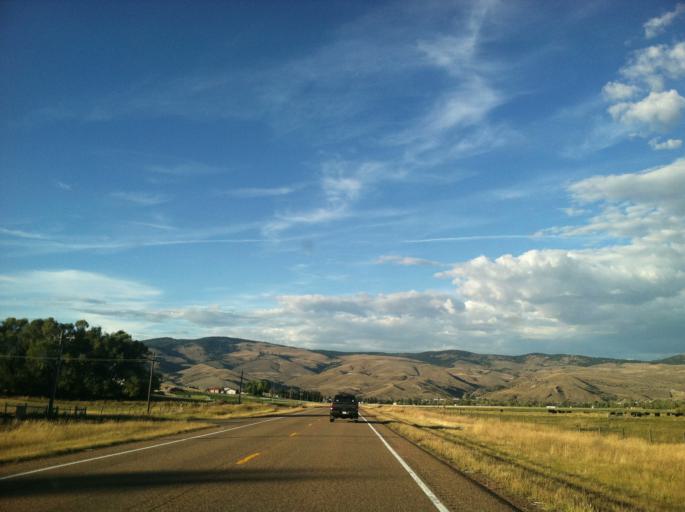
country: US
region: Montana
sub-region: Granite County
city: Philipsburg
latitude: 46.6447
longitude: -113.1646
